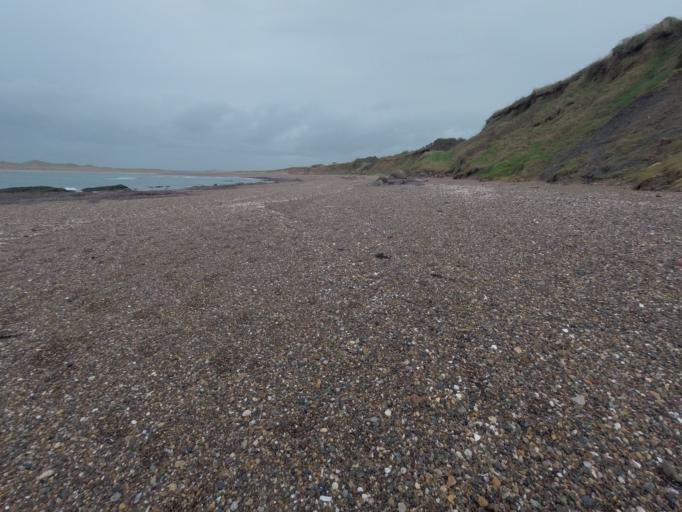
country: IE
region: Munster
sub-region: Waterford
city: Tra Mhor
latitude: 52.1422
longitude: -7.0933
